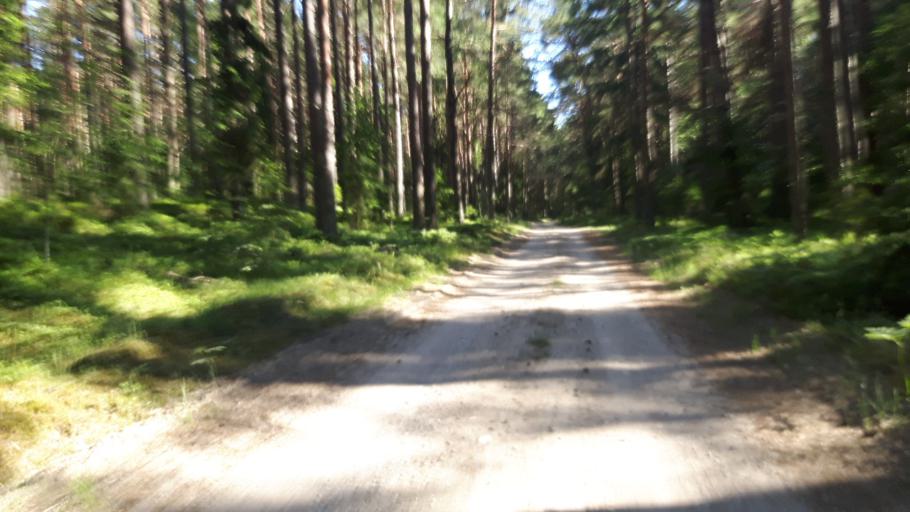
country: LV
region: Salacgrivas
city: Salacgriva
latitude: 57.7315
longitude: 24.3499
